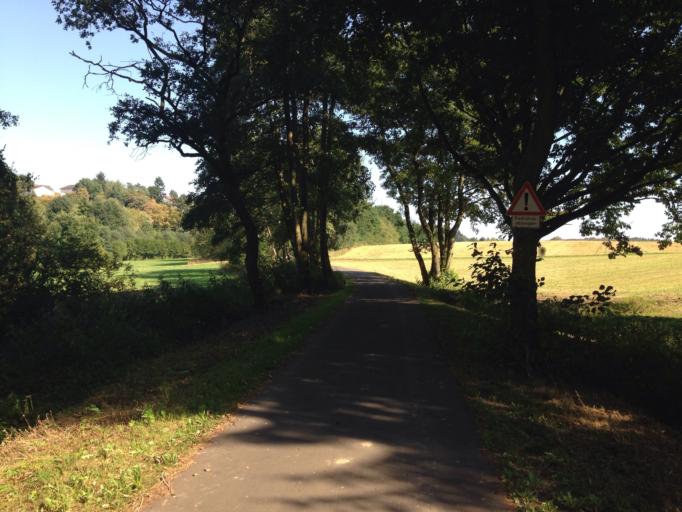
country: DE
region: Hesse
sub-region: Regierungsbezirk Giessen
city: Rabenau
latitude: 50.6638
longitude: 8.8820
